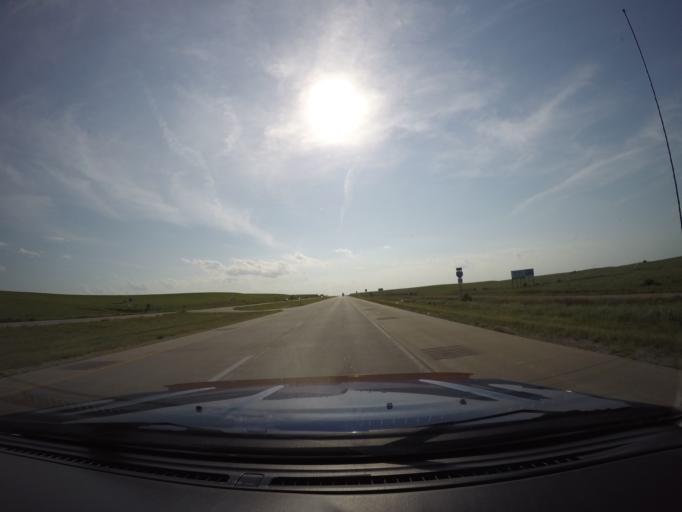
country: US
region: Kansas
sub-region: Wabaunsee County
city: Alma
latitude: 39.0655
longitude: -96.3898
